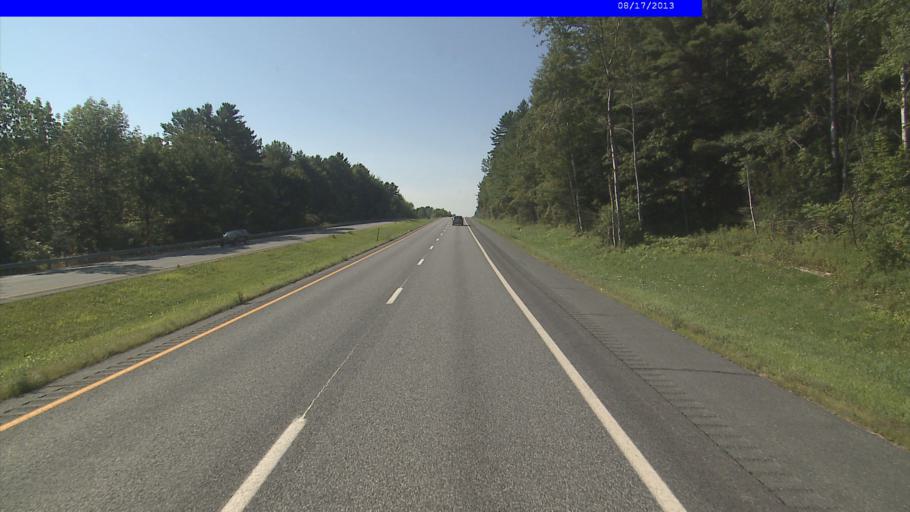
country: US
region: Vermont
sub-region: Windsor County
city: Windsor
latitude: 43.4807
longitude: -72.4067
